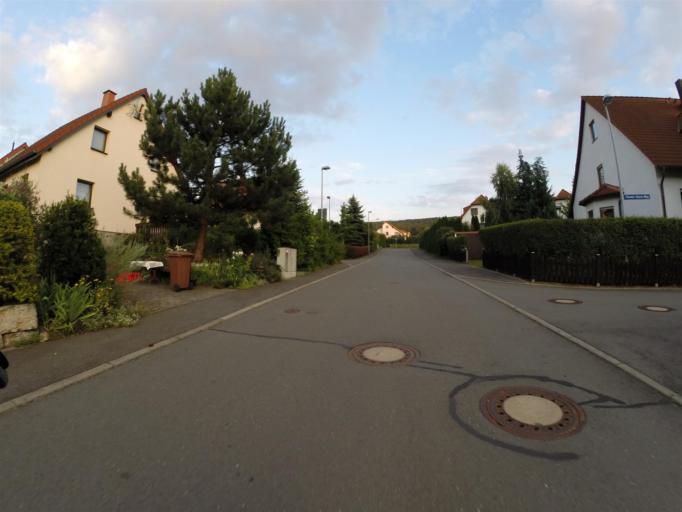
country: DE
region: Thuringia
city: Grosslobichau
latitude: 50.9308
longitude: 11.6565
